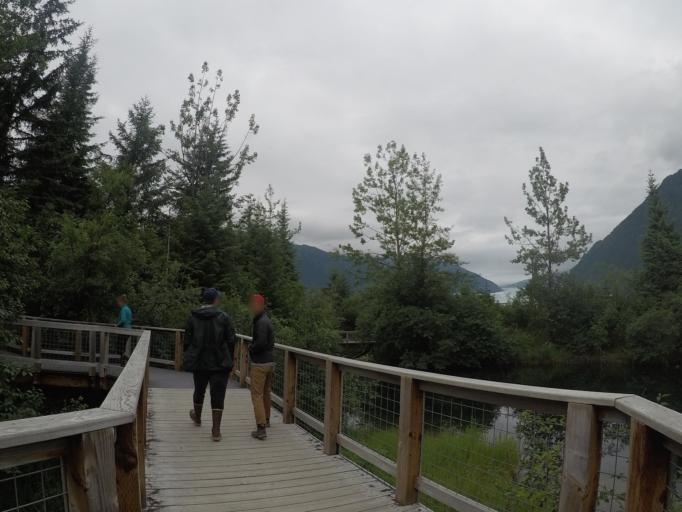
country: US
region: Alaska
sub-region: Juneau City and Borough
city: Juneau
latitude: 58.4159
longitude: -134.5477
